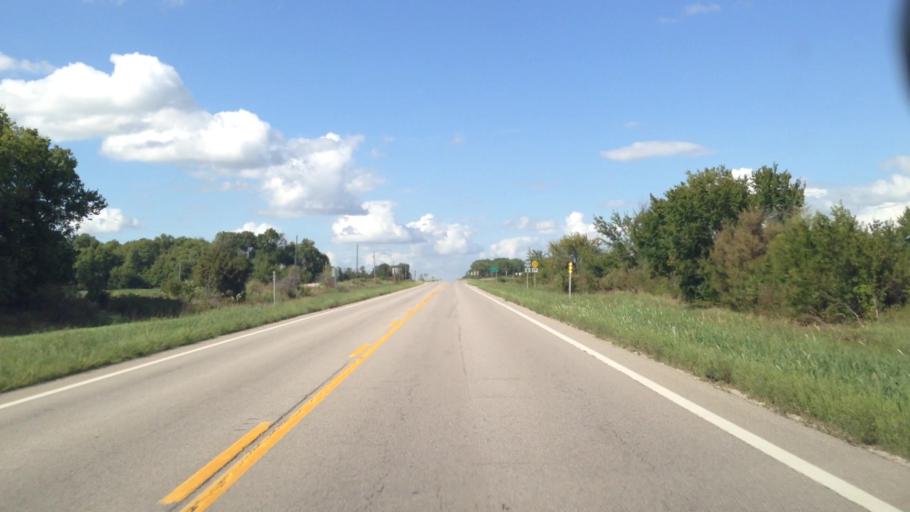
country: US
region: Kansas
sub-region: Neosho County
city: Erie
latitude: 37.7169
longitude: -95.1607
